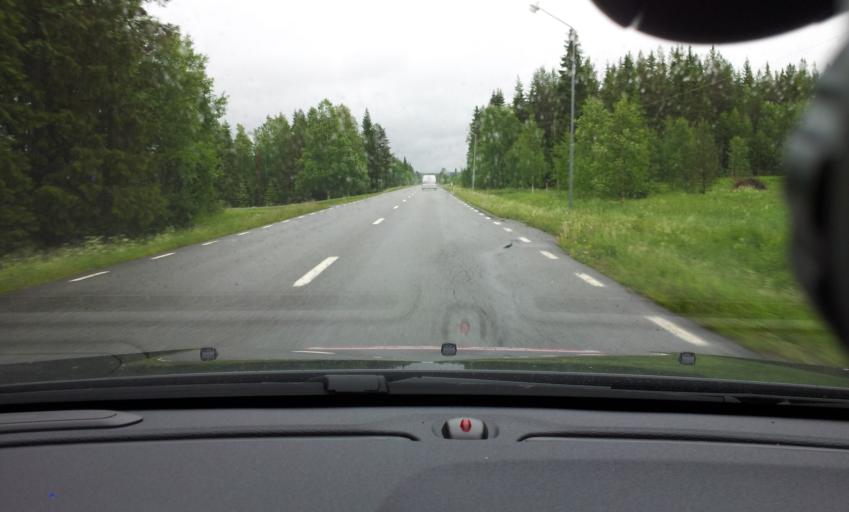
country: SE
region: Jaemtland
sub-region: Stroemsunds Kommun
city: Stroemsund
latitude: 63.5463
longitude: 15.4129
